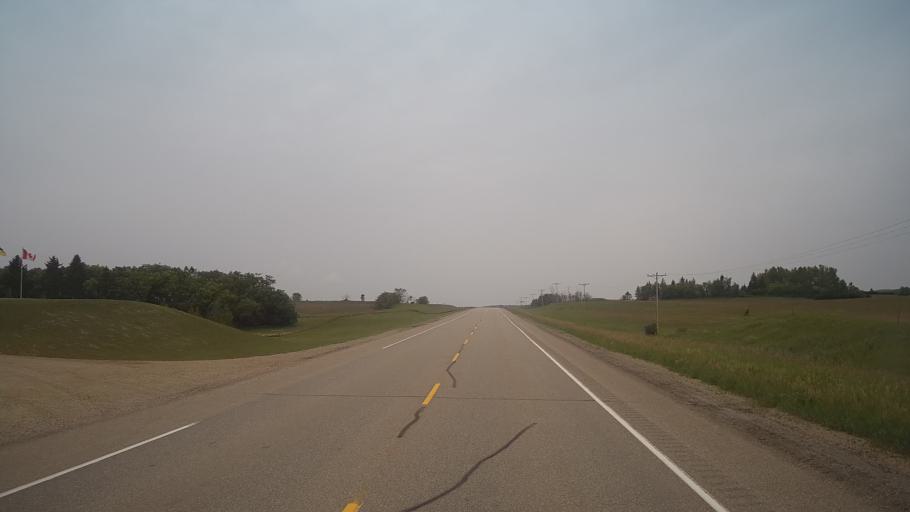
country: CA
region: Saskatchewan
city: Biggar
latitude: 52.0564
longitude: -107.8526
